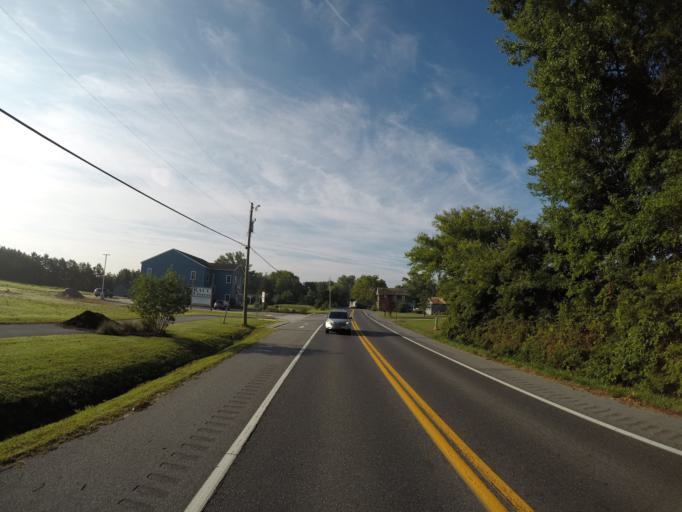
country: US
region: Delaware
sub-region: Sussex County
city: Selbyville
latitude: 38.4988
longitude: -75.1721
